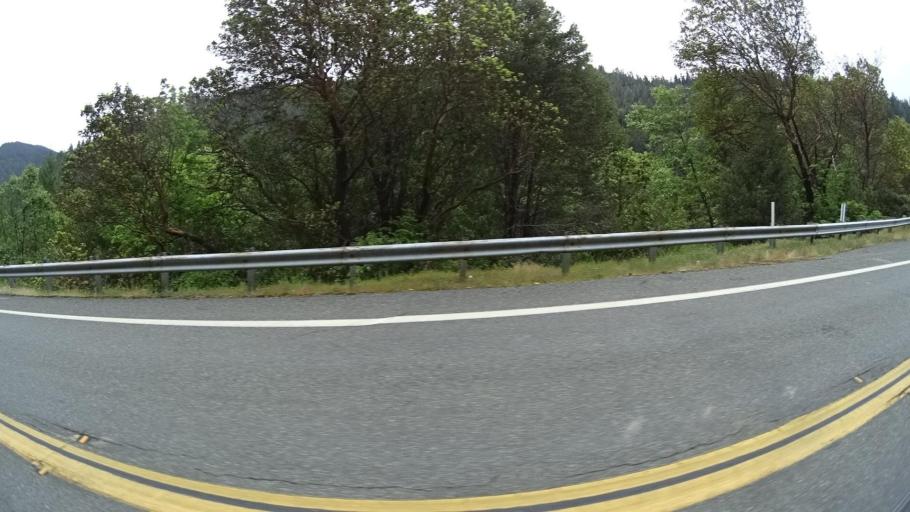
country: US
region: California
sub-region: Humboldt County
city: Willow Creek
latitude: 41.2780
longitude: -123.5916
